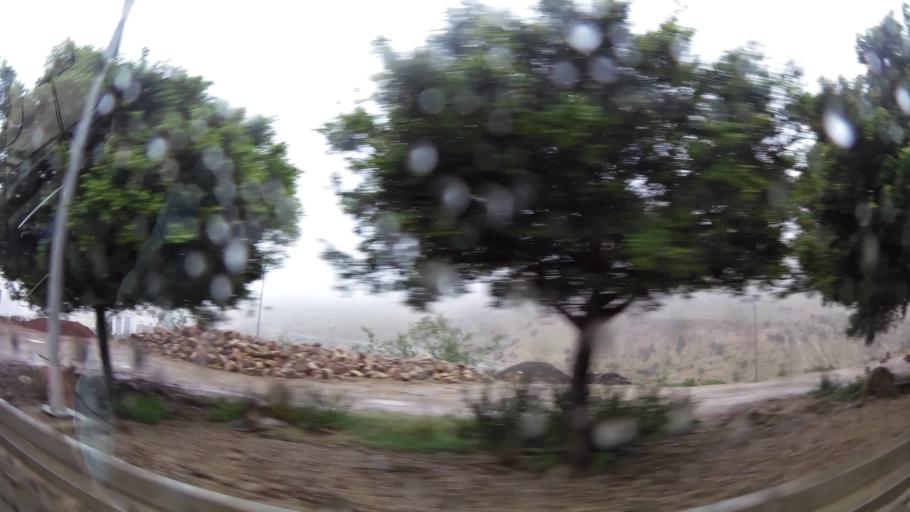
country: MA
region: Taza-Al Hoceima-Taounate
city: Tirhanimine
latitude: 35.2347
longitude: -3.9447
